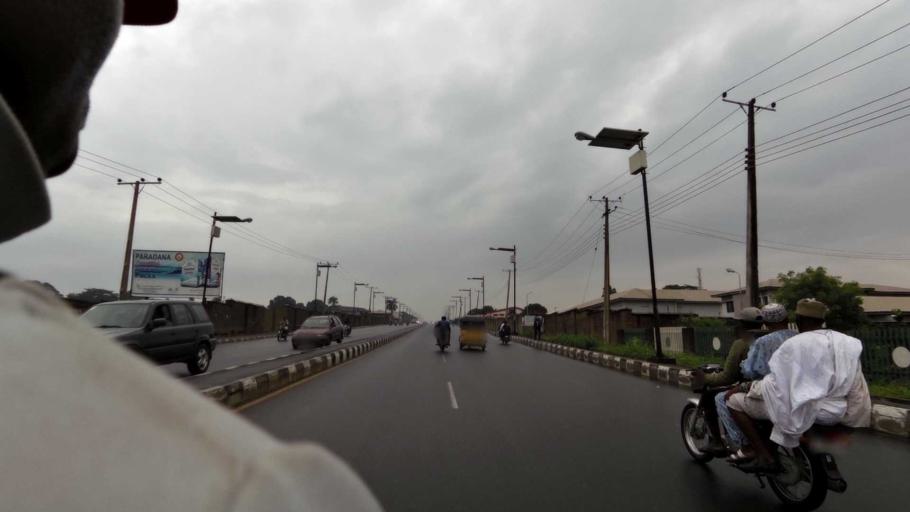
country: NG
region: Oyo
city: Ibadan
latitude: 7.3992
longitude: 3.9026
